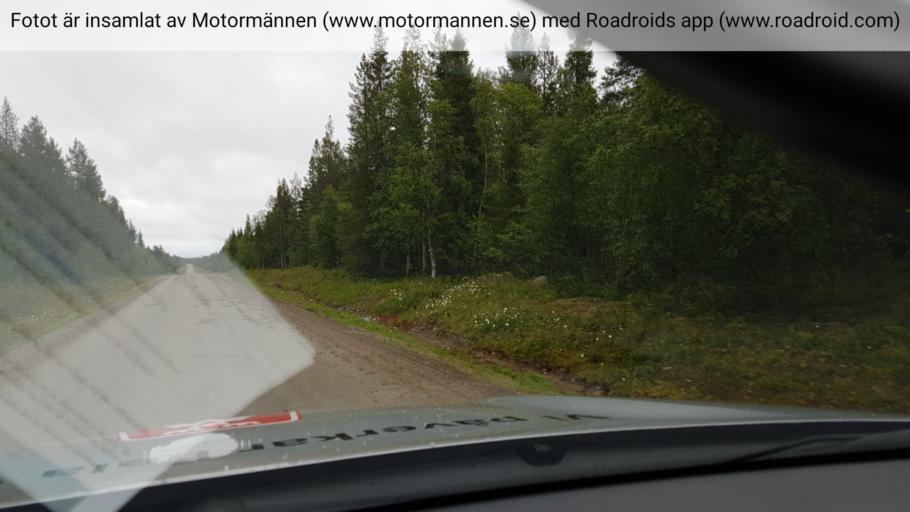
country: SE
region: Norrbotten
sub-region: Gallivare Kommun
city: Gaellivare
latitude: 66.7395
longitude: 20.7069
